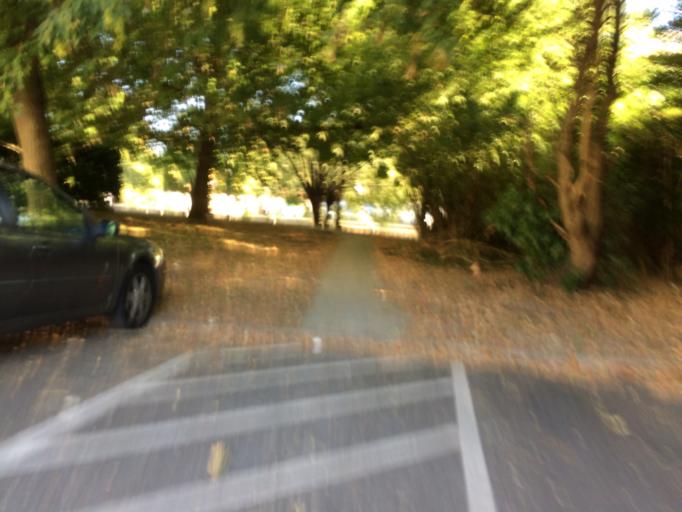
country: FR
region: Ile-de-France
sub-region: Departement de l'Essonne
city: Verrieres-le-Buisson
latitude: 48.7385
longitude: 2.2637
